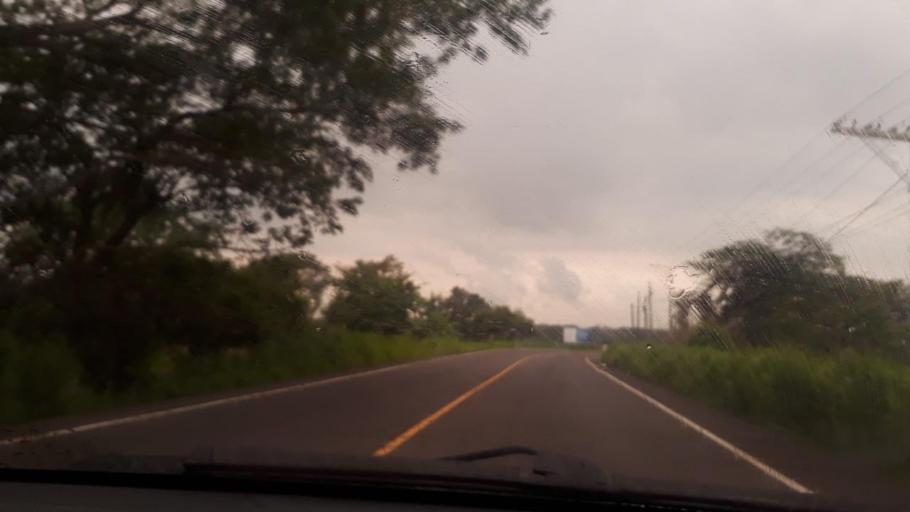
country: GT
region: Escuintla
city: Guanagazapa
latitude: 14.1013
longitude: -90.6154
